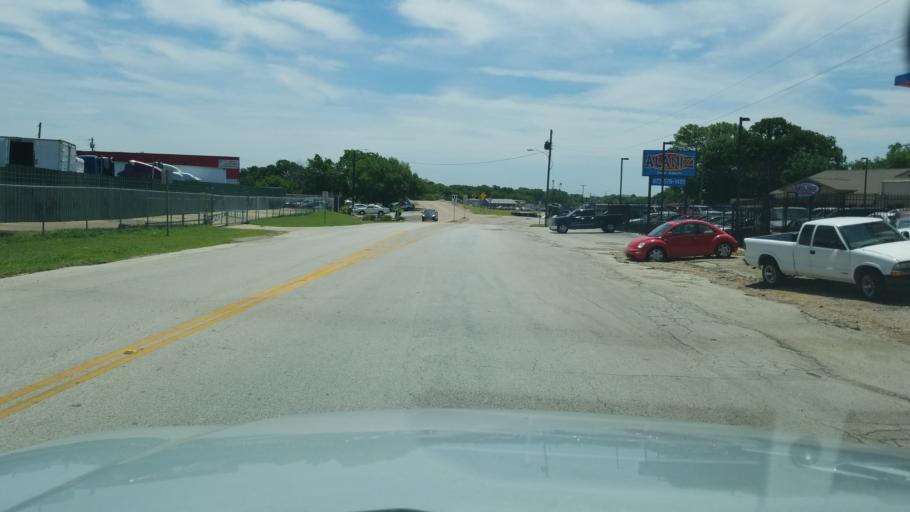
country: US
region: Texas
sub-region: Dallas County
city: Irving
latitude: 32.8073
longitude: -96.9238
